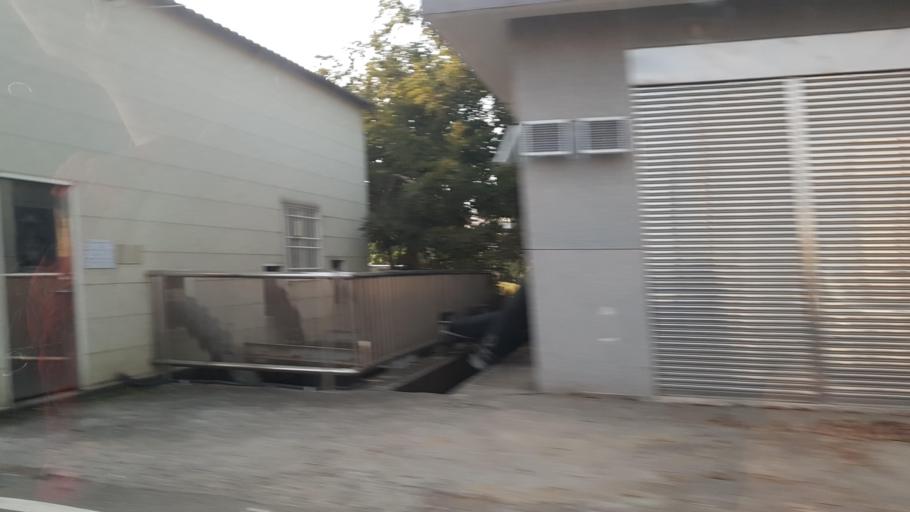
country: TW
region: Taiwan
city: Xinying
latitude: 23.3387
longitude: 120.3272
